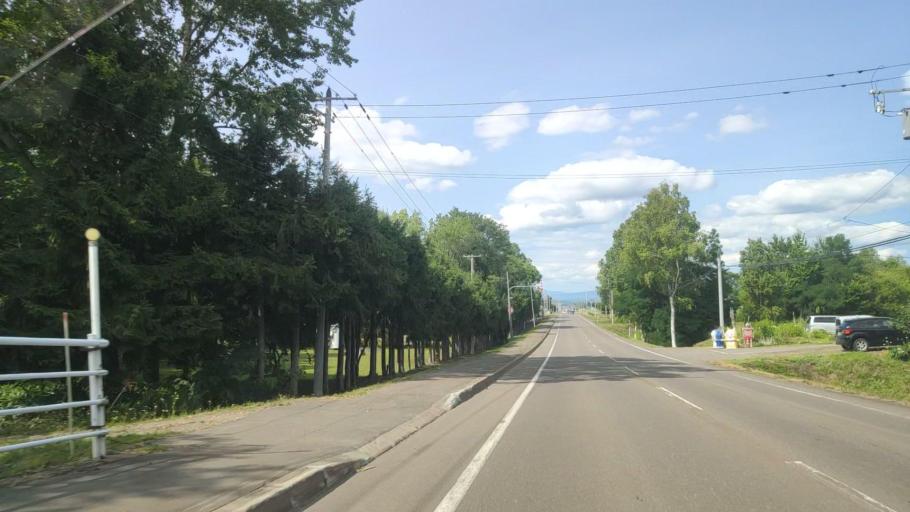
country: JP
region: Hokkaido
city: Nayoro
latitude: 44.2868
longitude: 142.4295
